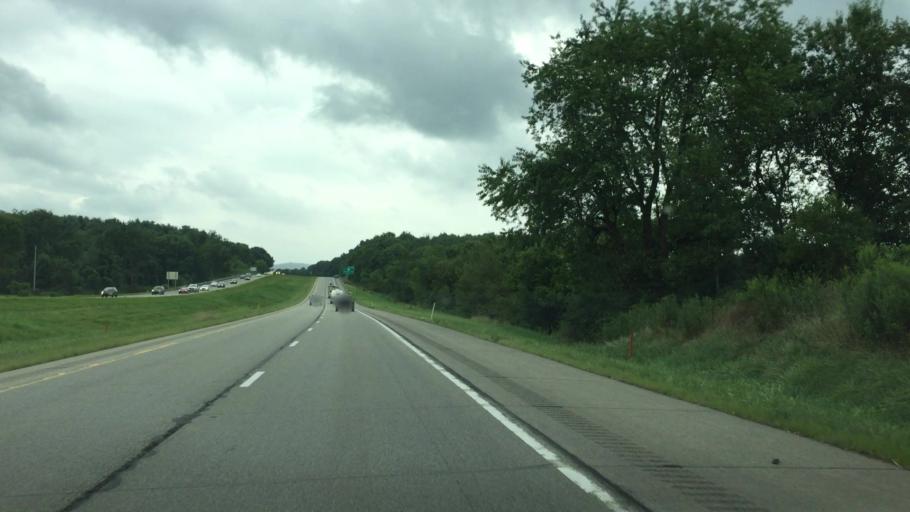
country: US
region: Pennsylvania
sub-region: Butler County
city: Slippery Rock
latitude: 41.0507
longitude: -80.1267
